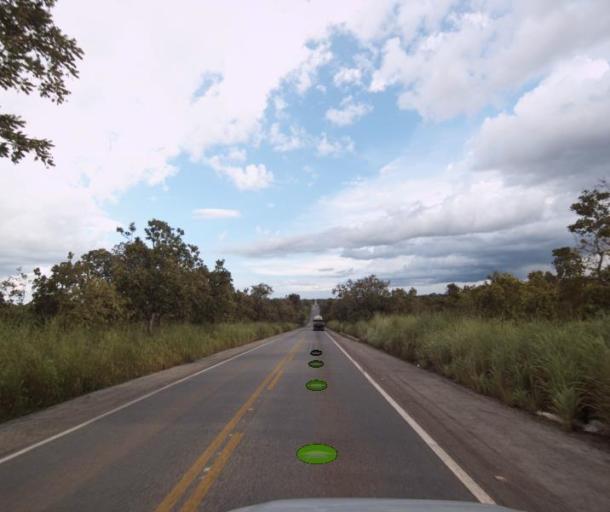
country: BR
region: Goias
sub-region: Porangatu
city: Porangatu
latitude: -13.3621
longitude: -49.1246
